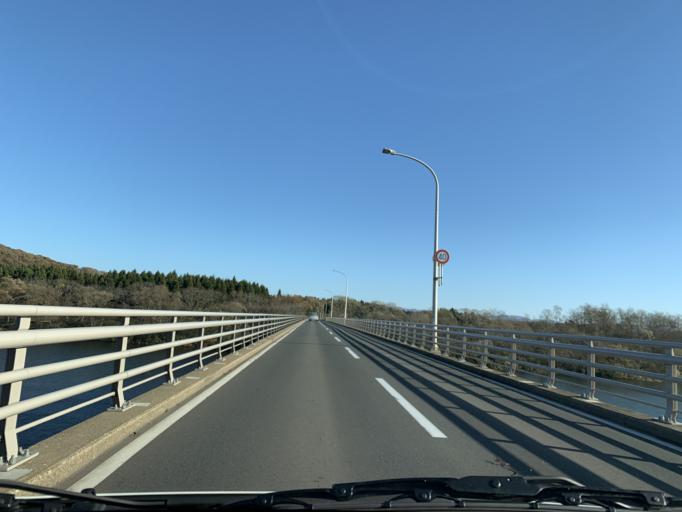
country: JP
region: Iwate
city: Kitakami
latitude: 39.2529
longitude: 141.1142
